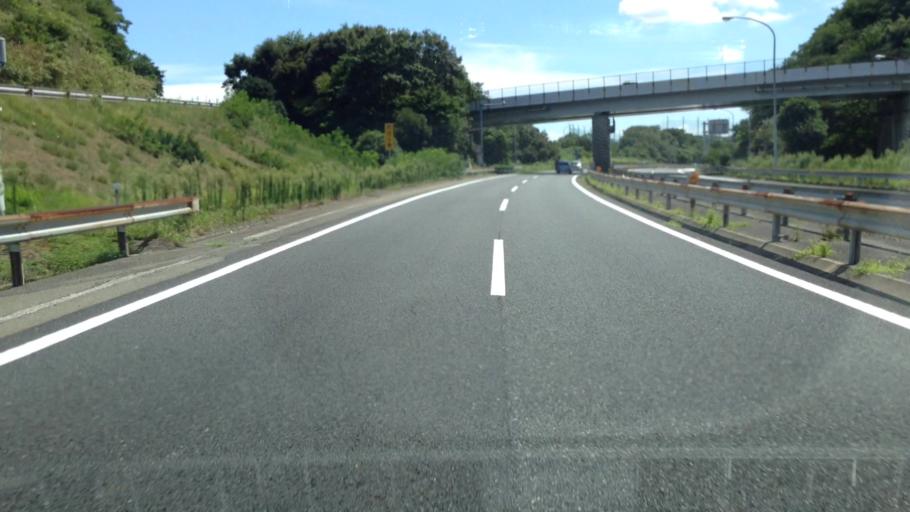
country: JP
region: Kanagawa
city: Yokosuka
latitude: 35.2779
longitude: 139.6334
